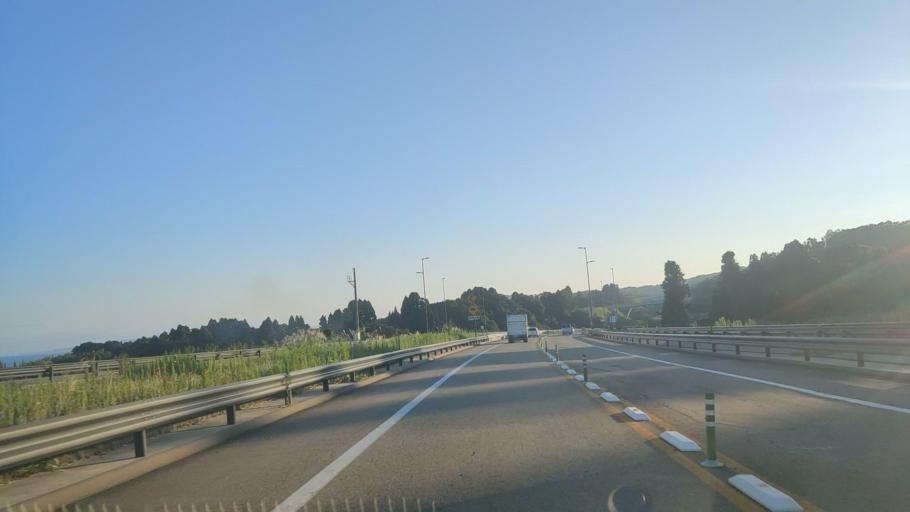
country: JP
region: Ishikawa
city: Nanao
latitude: 36.9613
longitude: 137.0471
